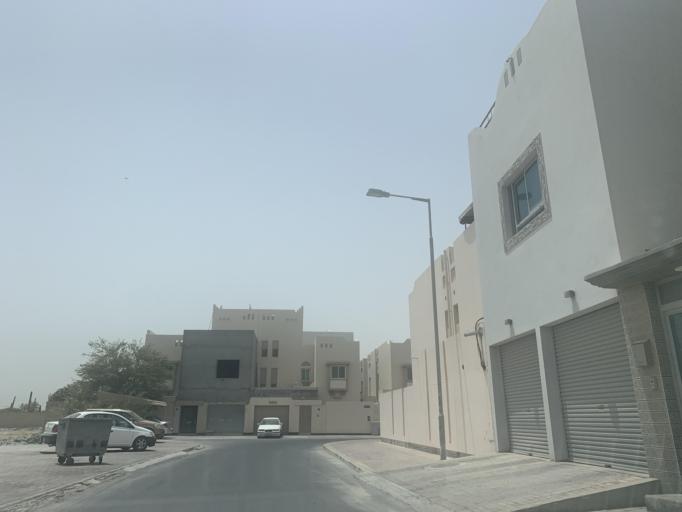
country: BH
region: Manama
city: Jidd Hafs
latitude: 26.2126
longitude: 50.5379
